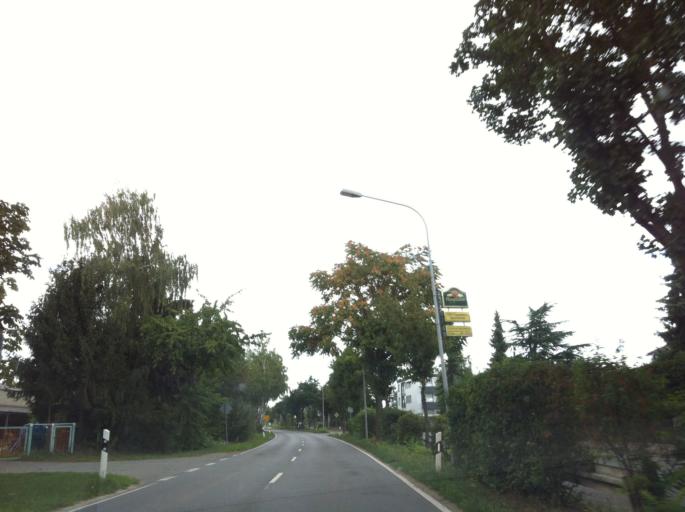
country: DE
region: Hesse
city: Pfungstadt
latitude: 49.8166
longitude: 8.5691
